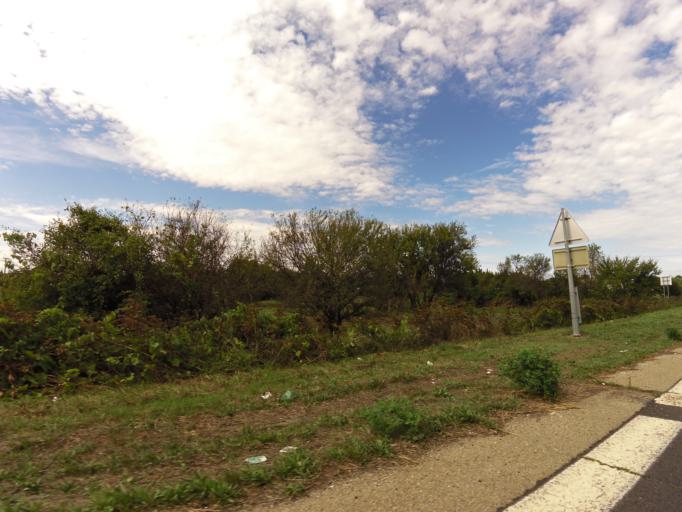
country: FR
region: Languedoc-Roussillon
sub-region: Departement du Gard
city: Aimargues
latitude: 43.6802
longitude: 4.2122
